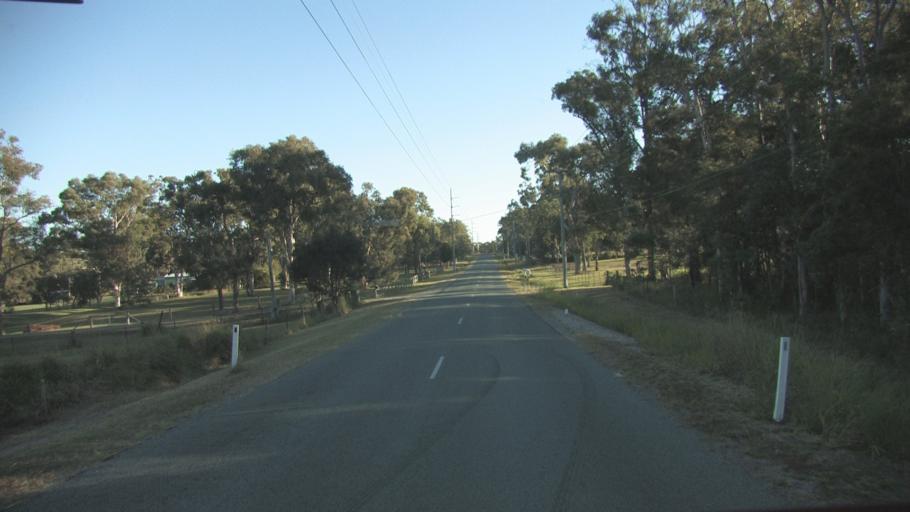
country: AU
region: Queensland
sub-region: Logan
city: Logan Reserve
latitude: -27.7316
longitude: 153.0927
